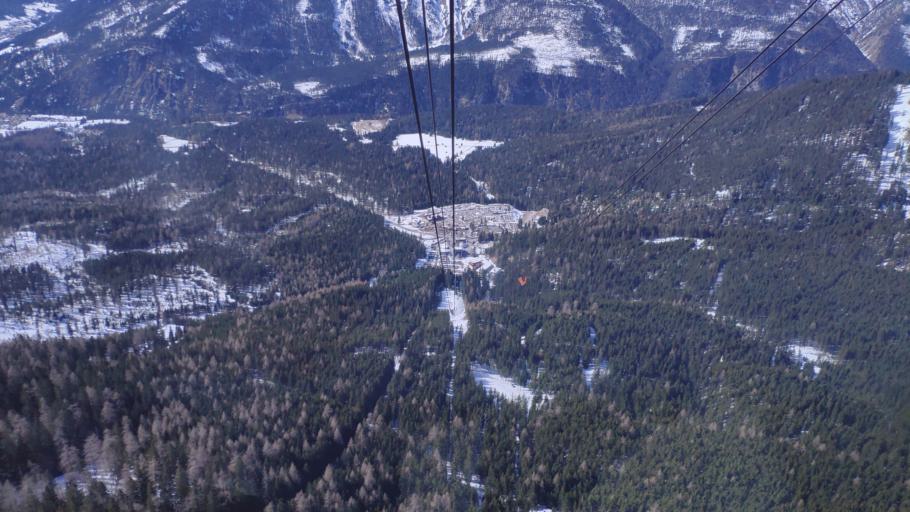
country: AT
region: Tyrol
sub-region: Politischer Bezirk Reutte
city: Ehrwald
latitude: 47.4246
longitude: 10.9590
